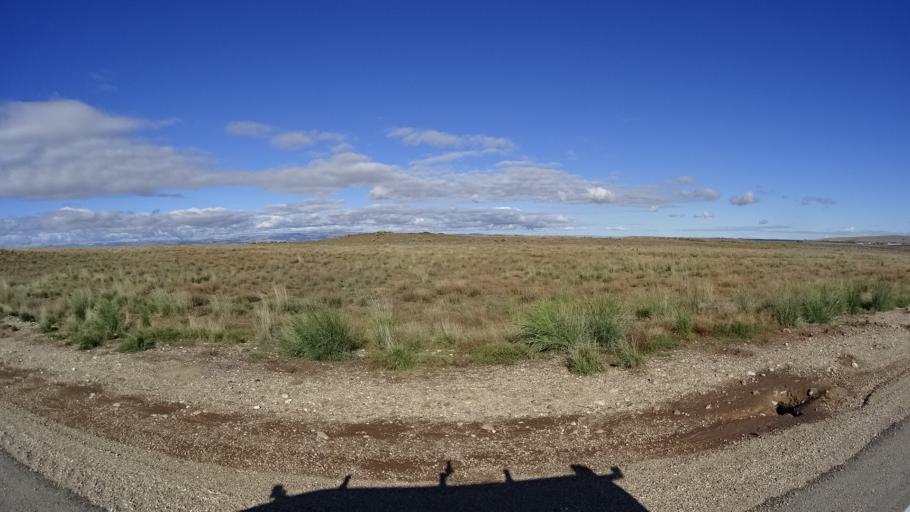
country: US
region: Idaho
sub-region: Ada County
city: Kuna
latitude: 43.3852
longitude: -116.4139
